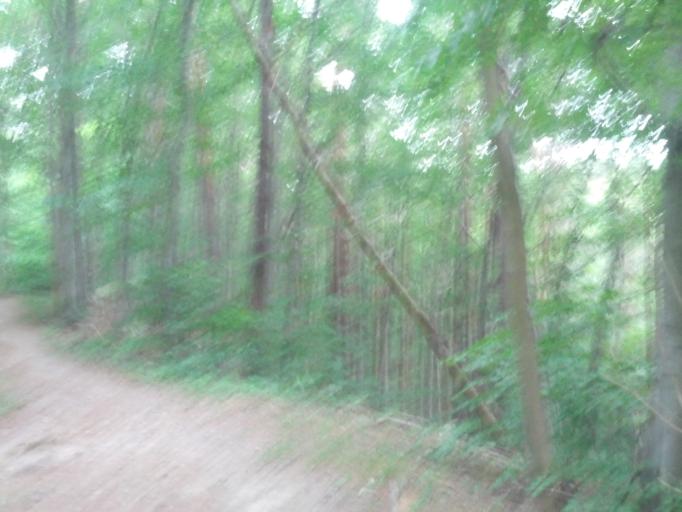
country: DE
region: Thuringia
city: Eisenach
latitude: 50.9643
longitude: 10.3379
